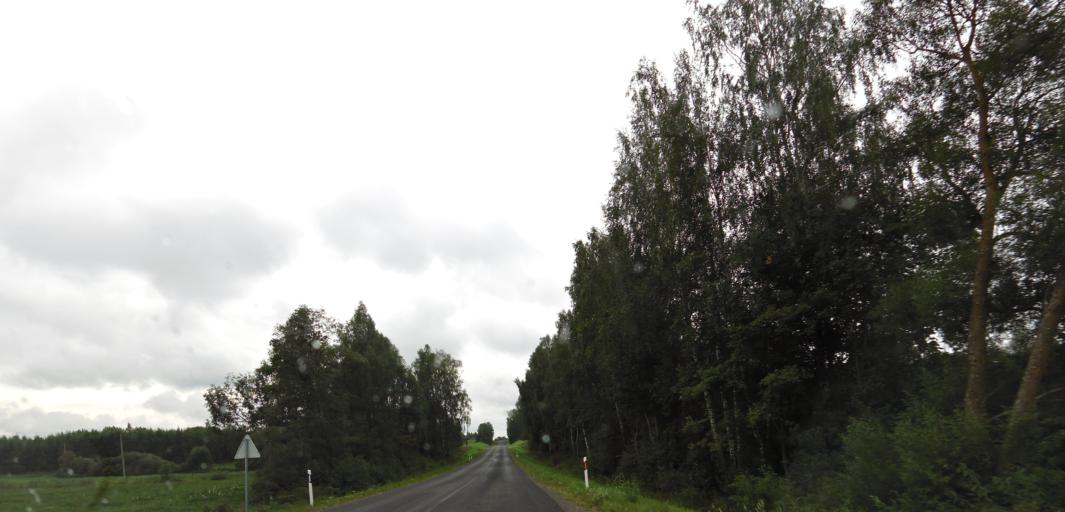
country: LT
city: Moletai
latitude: 55.2578
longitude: 25.3584
